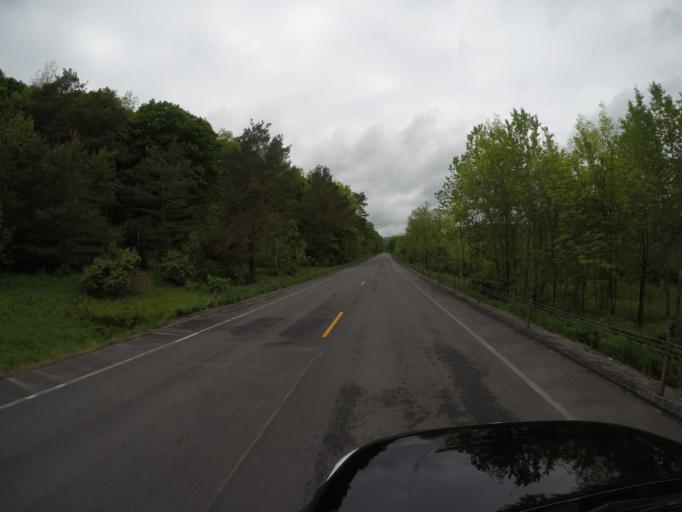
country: US
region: New York
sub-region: Delaware County
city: Delhi
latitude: 42.2417
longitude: -74.7994
